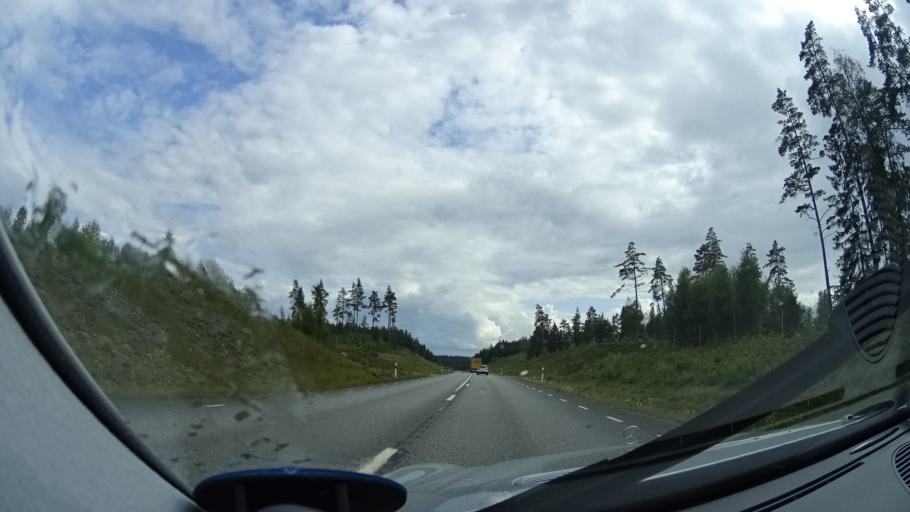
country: SE
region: Blekinge
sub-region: Karlshamns Kommun
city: Svangsta
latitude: 56.3318
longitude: 14.8866
